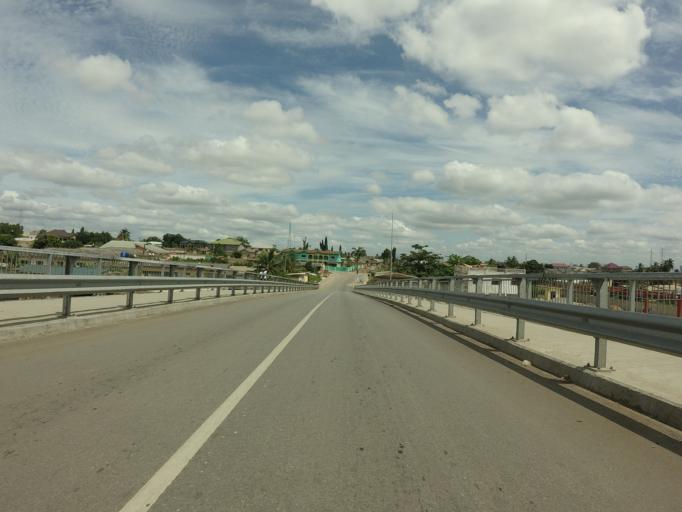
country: GH
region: Central
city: Kasoa
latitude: 5.5388
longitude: -0.4000
